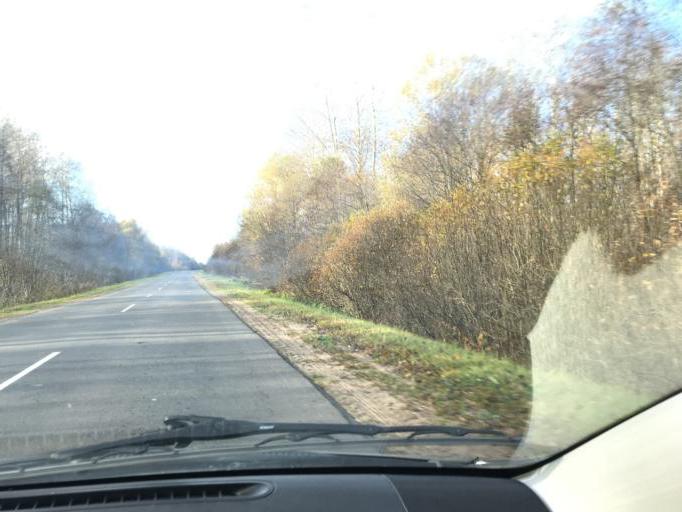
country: BY
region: Vitebsk
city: Haradok
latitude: 55.4241
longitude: 29.8053
